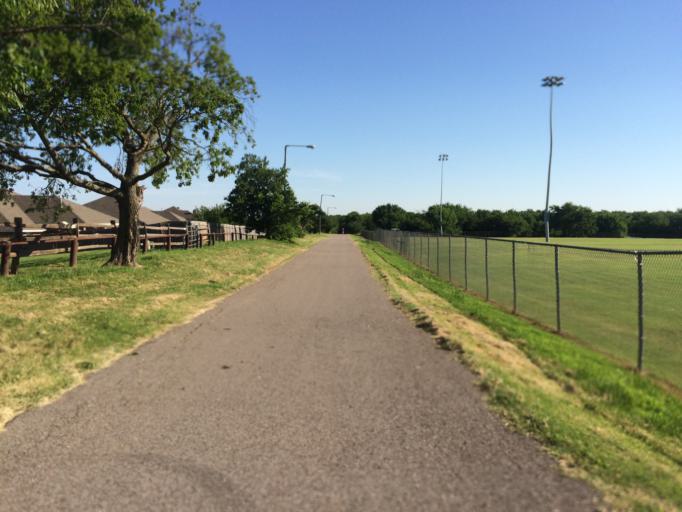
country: US
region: Oklahoma
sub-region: Cleveland County
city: Norman
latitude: 35.2361
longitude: -97.4323
